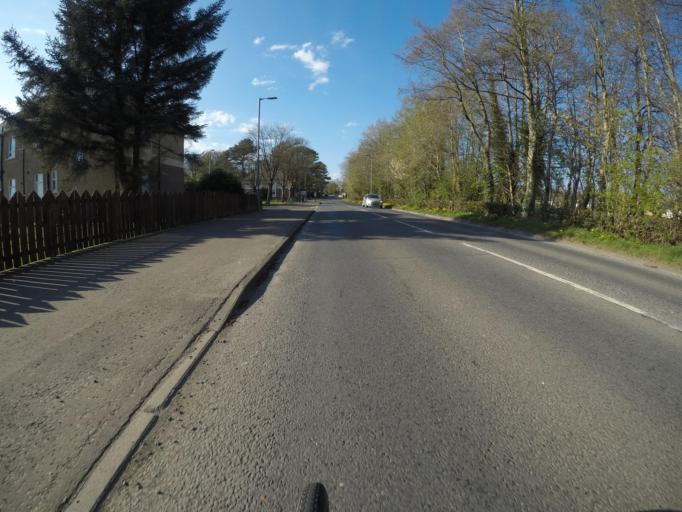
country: GB
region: Scotland
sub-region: North Ayrshire
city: Kilwinning
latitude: 55.6489
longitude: -4.6882
